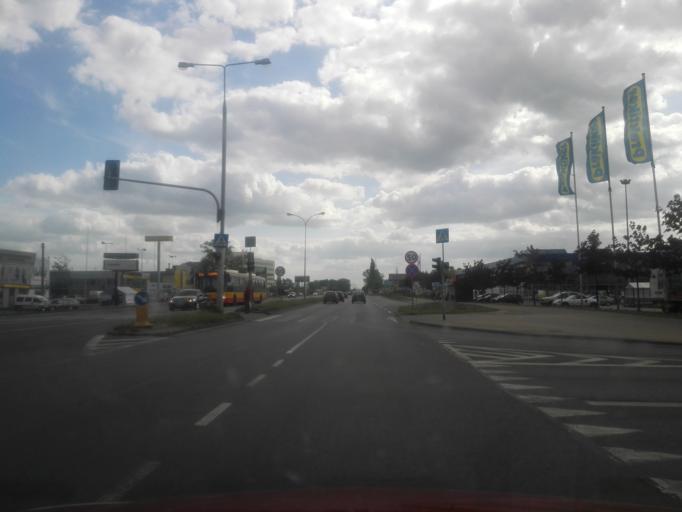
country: PL
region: Masovian Voivodeship
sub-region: Powiat wolominski
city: Zabki
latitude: 52.3034
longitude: 21.0888
